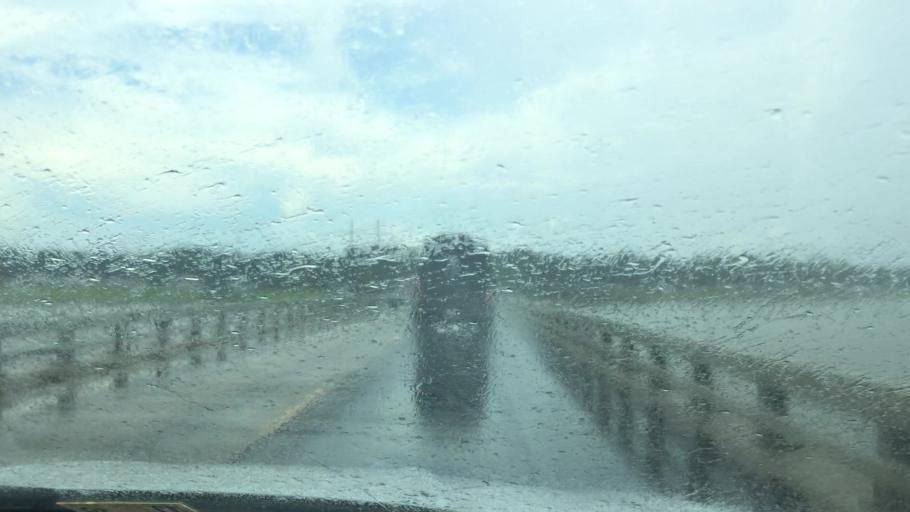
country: US
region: Virginia
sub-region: Lancaster County
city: Kilmarnock
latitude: 37.6164
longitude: -76.4313
